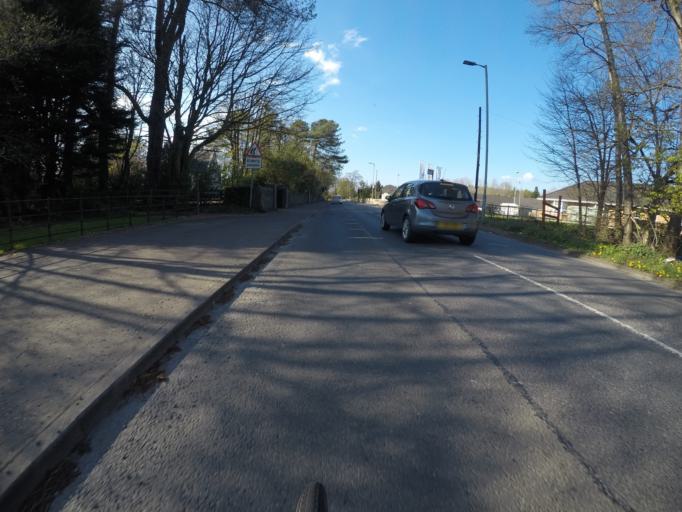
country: GB
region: Scotland
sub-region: North Ayrshire
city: Kilwinning
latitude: 55.6498
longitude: -4.6886
